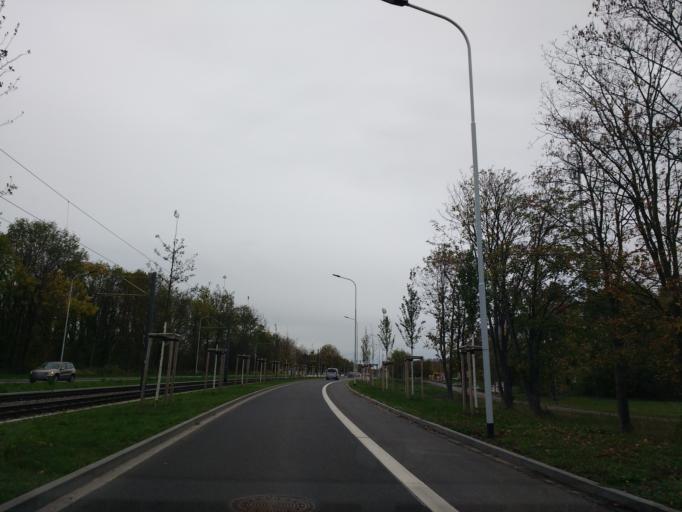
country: DE
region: Saxony-Anhalt
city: Halle Neustadt
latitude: 51.4918
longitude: 11.9436
